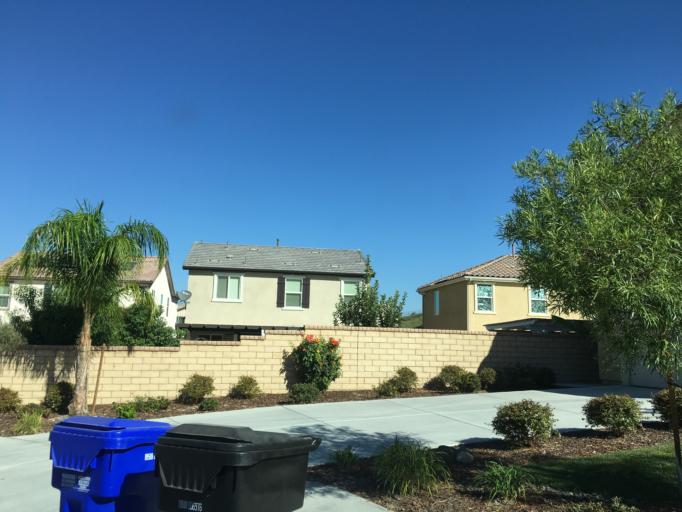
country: US
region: California
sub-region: Los Angeles County
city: Santa Clarita
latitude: 34.4433
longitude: -118.4821
